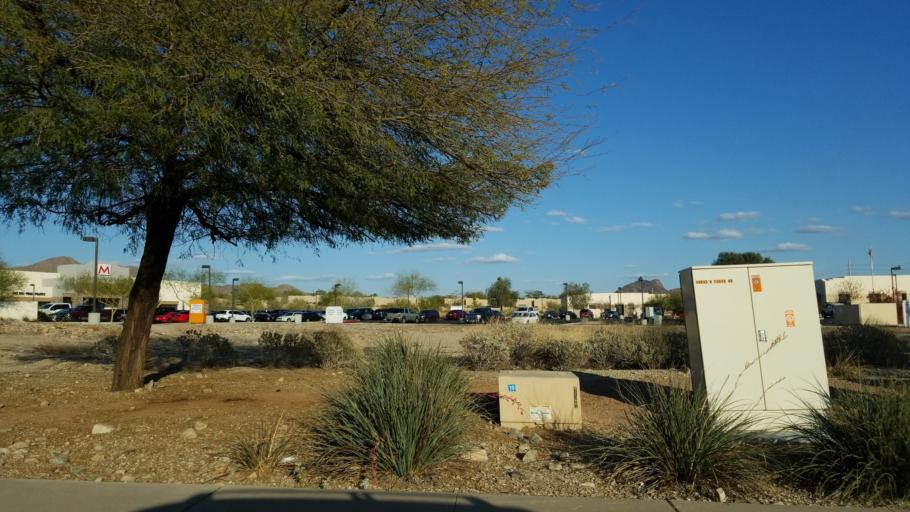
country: US
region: Arizona
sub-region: Maricopa County
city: Scottsdale
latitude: 33.5834
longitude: -111.8307
